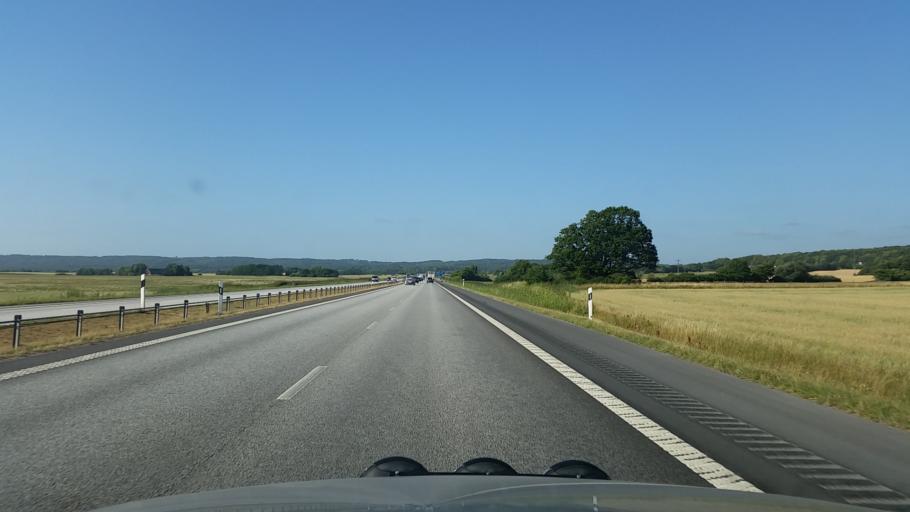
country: SE
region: Skane
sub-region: Angelholms Kommun
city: AEngelholm
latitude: 56.2968
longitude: 12.9052
